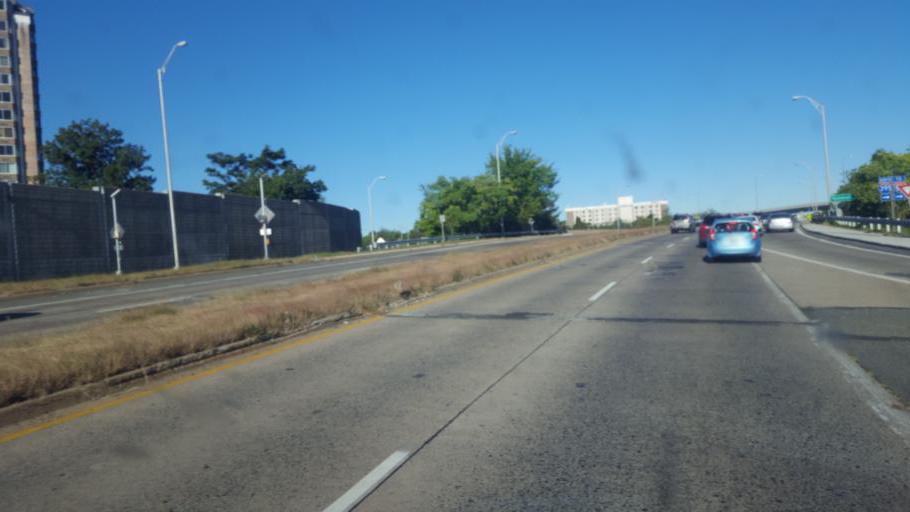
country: US
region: Virginia
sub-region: Fairfax County
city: Lincolnia
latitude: 38.8150
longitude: -77.1367
